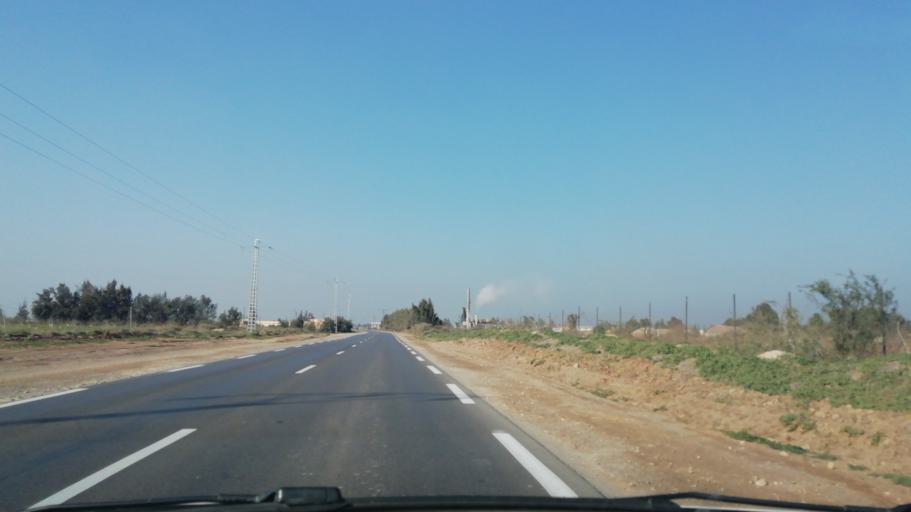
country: DZ
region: Mostaganem
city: Mostaganem
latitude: 35.7520
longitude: 0.0393
